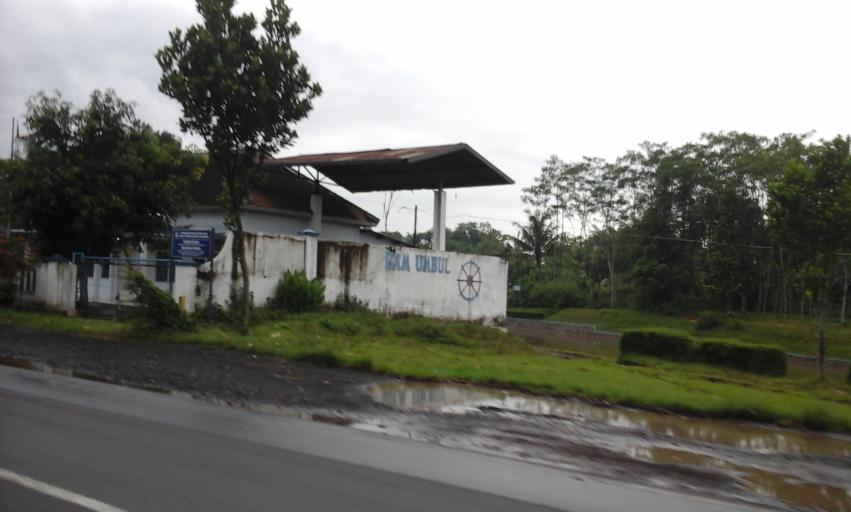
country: ID
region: East Java
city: Krajan Baru
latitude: -8.0942
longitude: 113.2631
